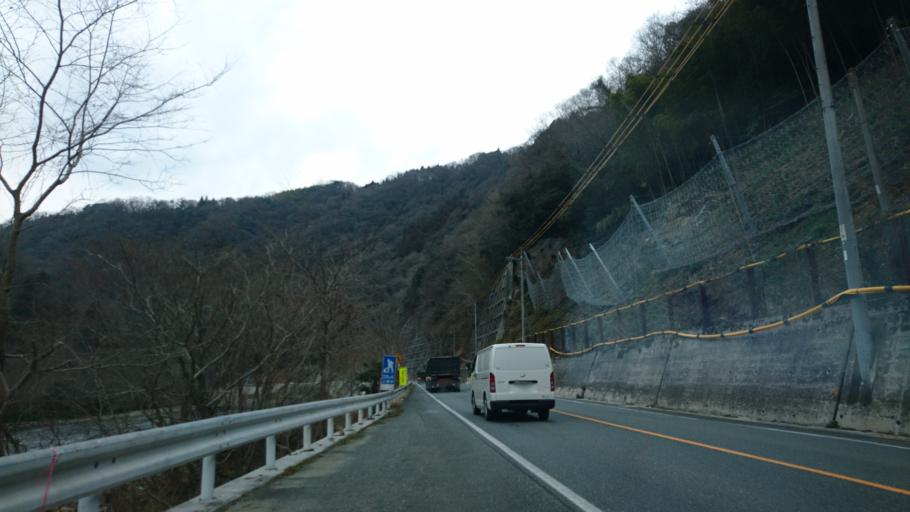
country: JP
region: Okayama
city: Niimi
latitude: 34.9108
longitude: 133.5325
